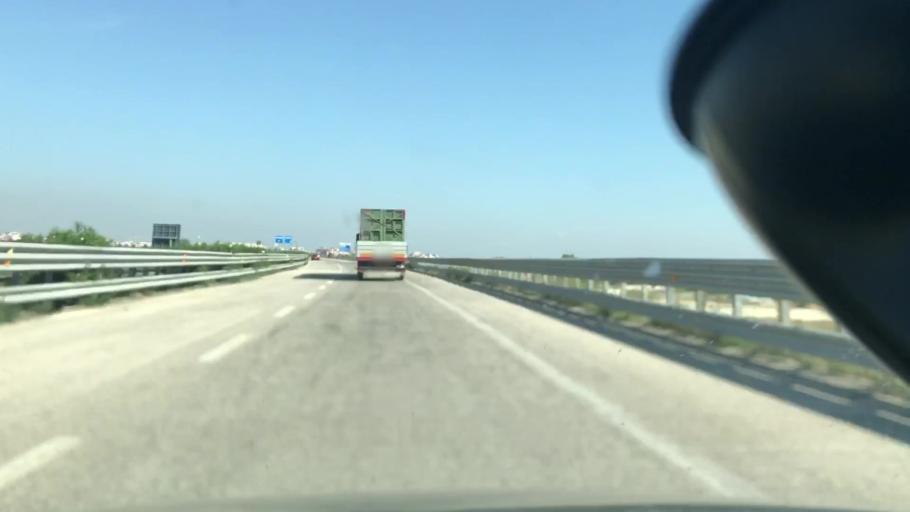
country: IT
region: Apulia
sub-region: Provincia di Foggia
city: Foggia
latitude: 41.4225
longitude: 15.5590
